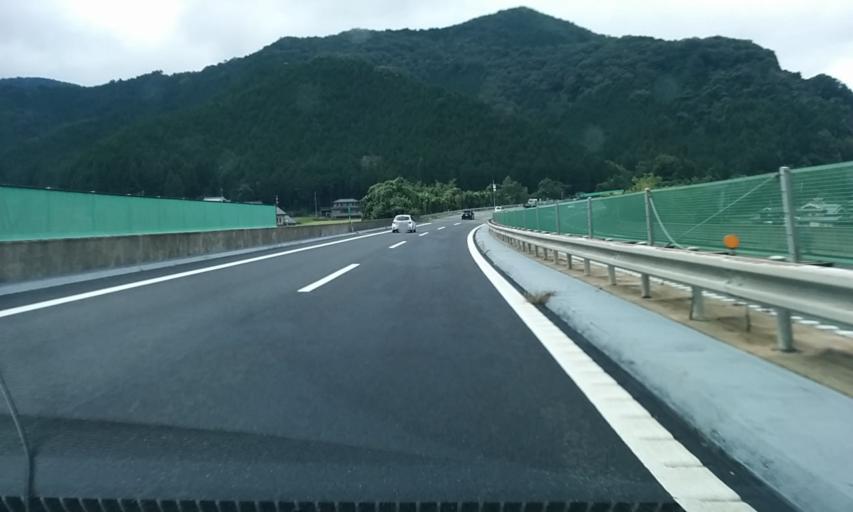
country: JP
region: Kyoto
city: Fukuchiyama
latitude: 35.2002
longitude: 135.1569
